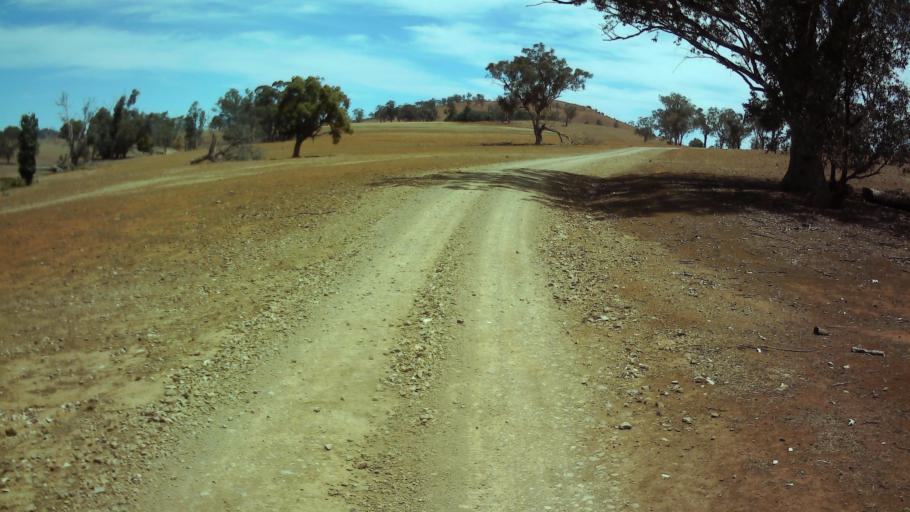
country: AU
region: New South Wales
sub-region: Weddin
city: Grenfell
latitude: -33.7454
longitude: 148.1715
